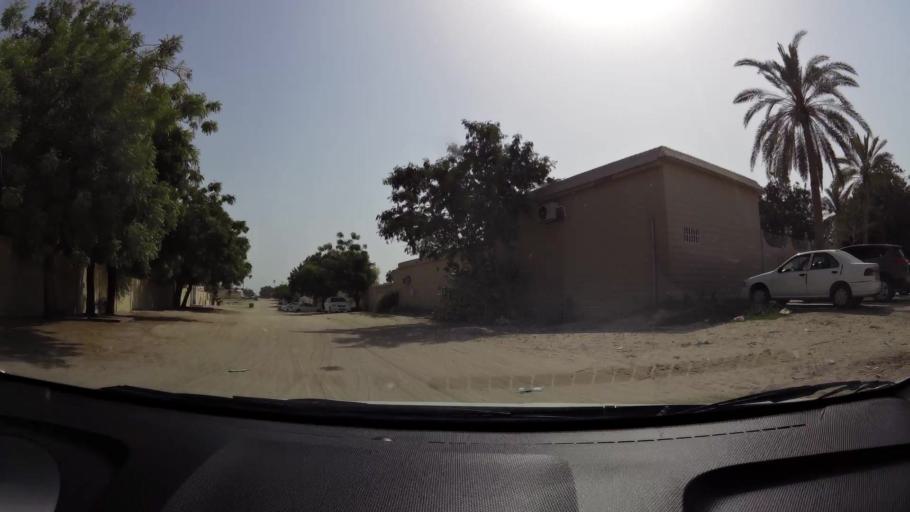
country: AE
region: Ash Shariqah
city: Sharjah
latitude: 25.3431
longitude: 55.4168
